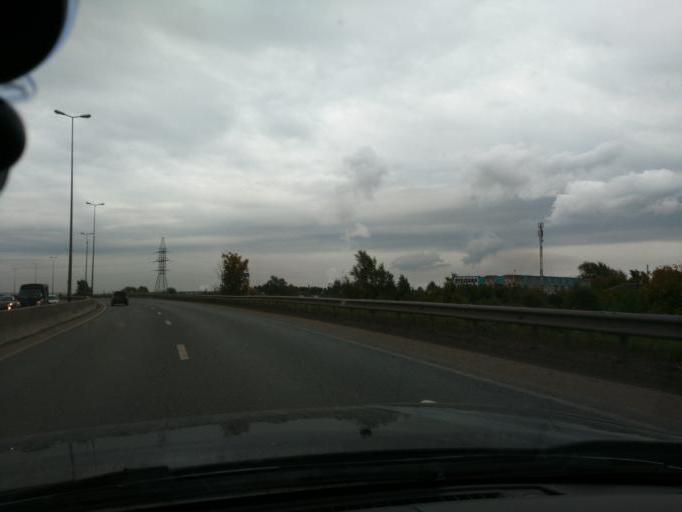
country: RU
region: Perm
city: Kondratovo
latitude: 57.9457
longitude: 56.1254
